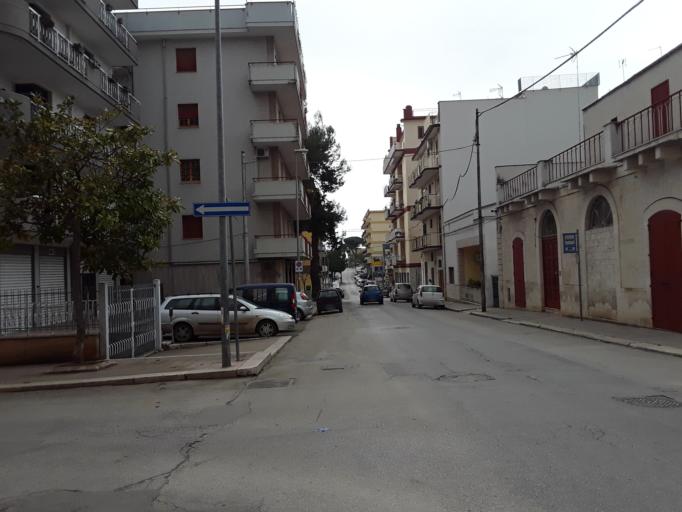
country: IT
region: Apulia
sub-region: Provincia di Bari
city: Ruvo di Puglia
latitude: 41.1194
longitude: 16.4796
